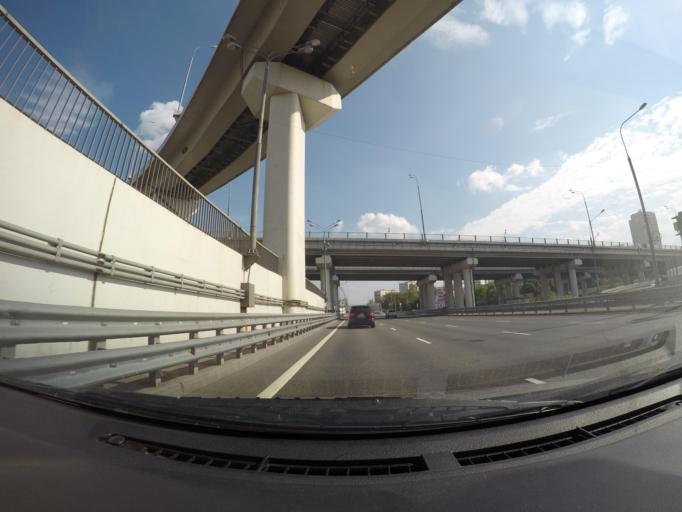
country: RU
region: Moscow
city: Novokhovrino
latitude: 55.8672
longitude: 37.5122
